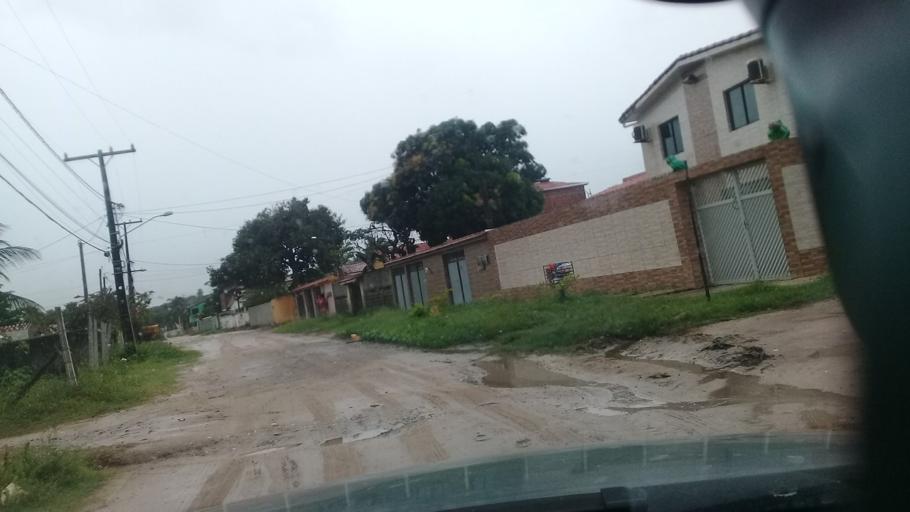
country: BR
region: Pernambuco
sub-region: Itamaraca
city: Itamaraca
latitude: -7.7564
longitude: -34.8277
